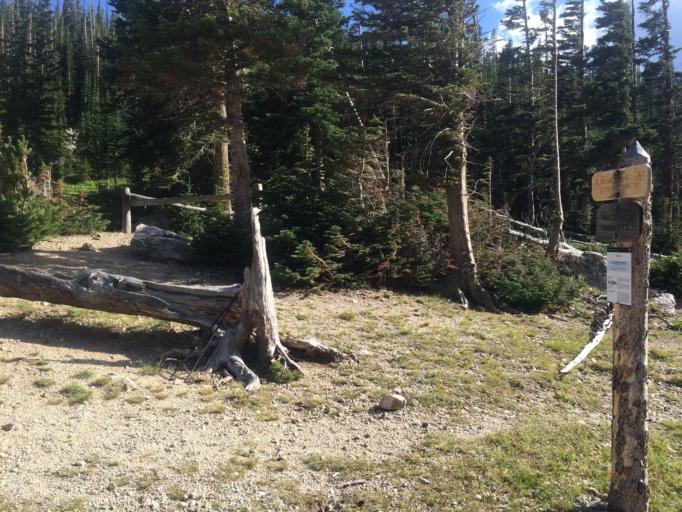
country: US
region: Colorado
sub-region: Larimer County
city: Estes Park
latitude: 40.1768
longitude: -105.6228
